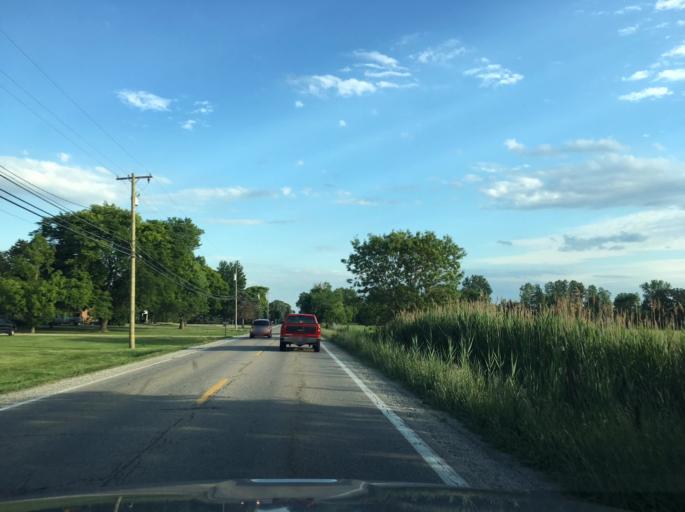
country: US
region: Michigan
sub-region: Macomb County
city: Romeo
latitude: 42.7407
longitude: -82.9604
